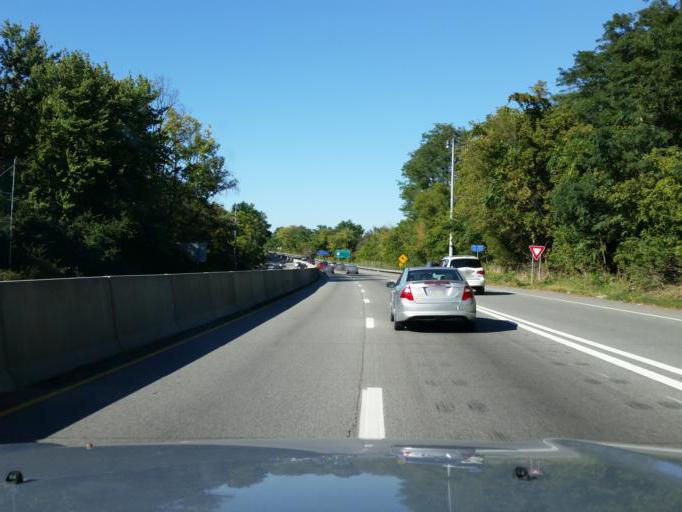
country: US
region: Pennsylvania
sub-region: Chester County
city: West Chester
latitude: 39.9585
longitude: -75.5799
